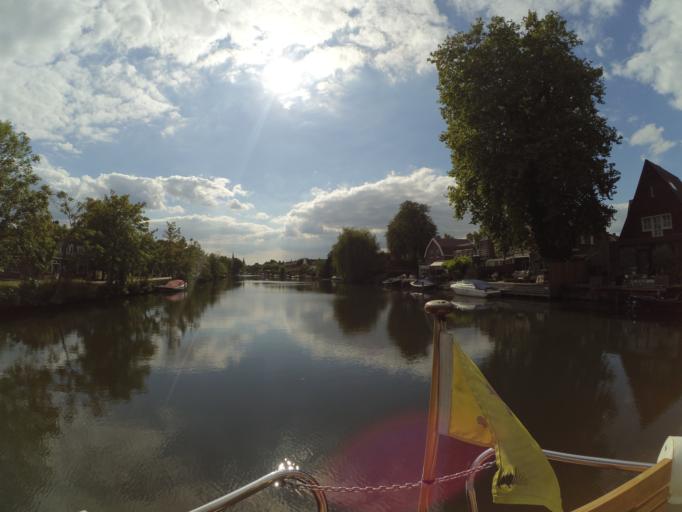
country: NL
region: Utrecht
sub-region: Stichtse Vecht
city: Breukelen
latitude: 52.1792
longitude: 5.0043
